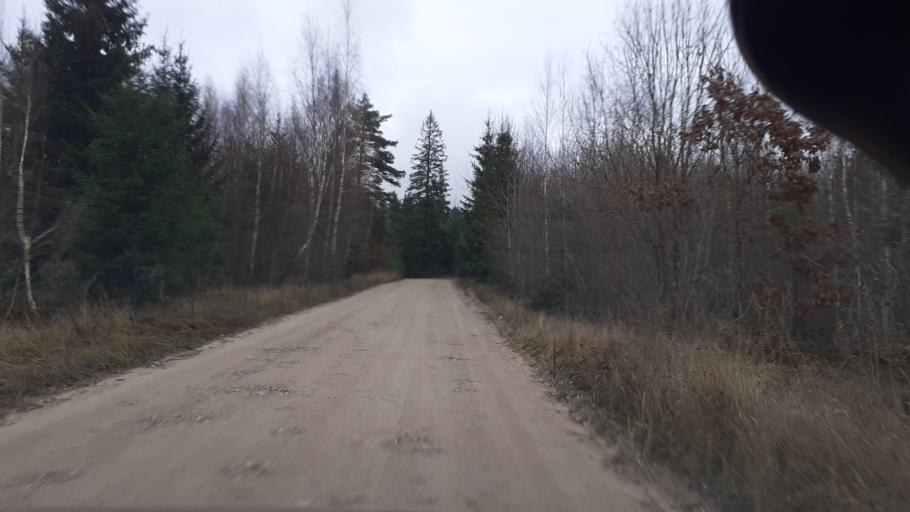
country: LV
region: Kuldigas Rajons
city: Kuldiga
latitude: 57.0313
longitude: 21.8724
